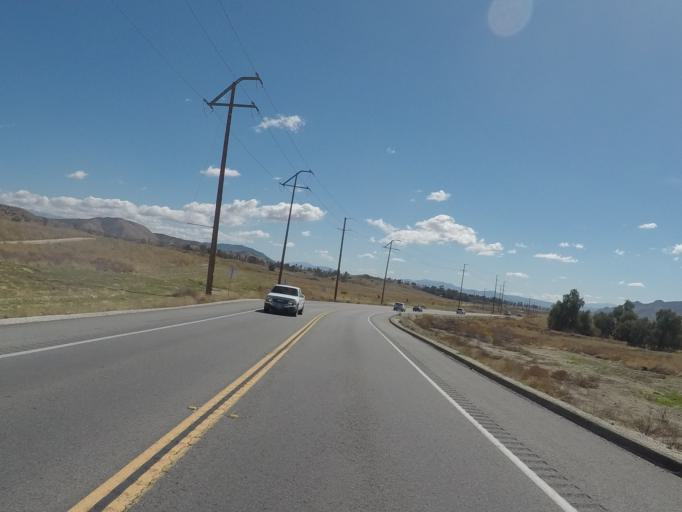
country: US
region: California
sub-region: Riverside County
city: Lakeview
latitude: 33.9055
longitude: -117.0895
